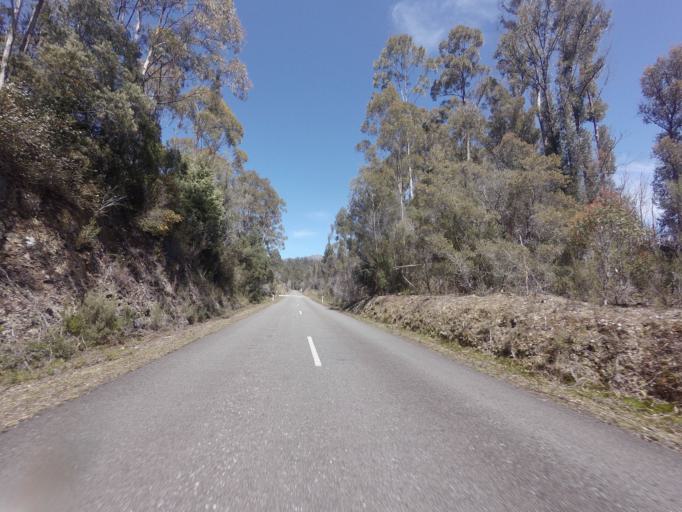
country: AU
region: Tasmania
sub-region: Huon Valley
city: Geeveston
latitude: -42.8327
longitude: 146.2682
